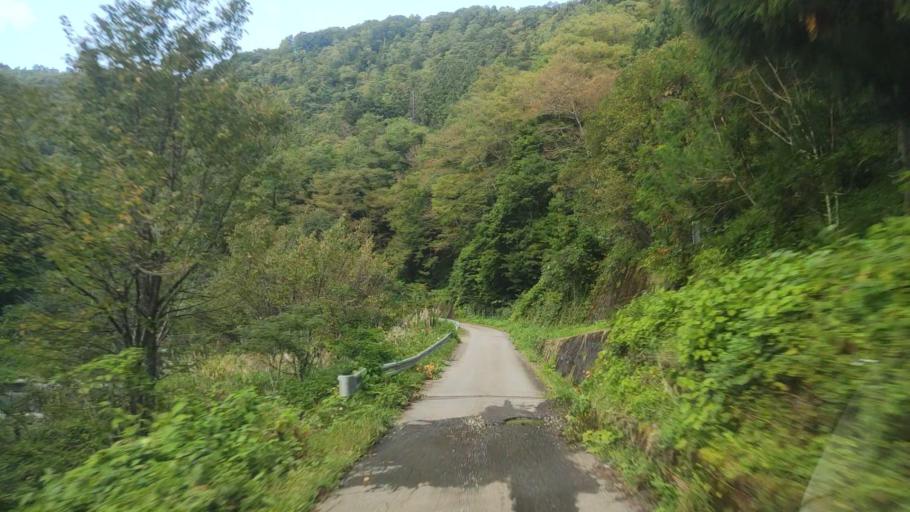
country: JP
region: Gifu
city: Takayama
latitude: 36.3089
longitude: 137.0933
